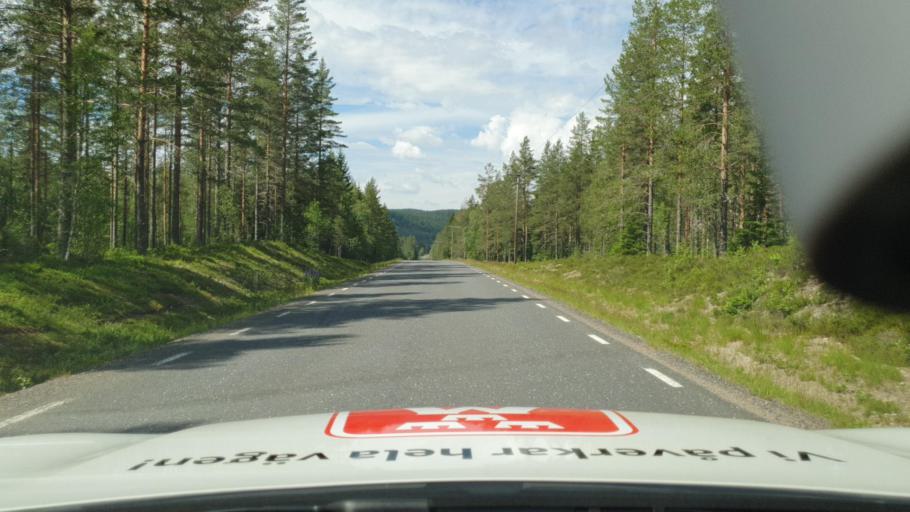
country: SE
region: Vaermland
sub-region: Torsby Kommun
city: Torsby
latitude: 60.5614
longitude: 12.7581
